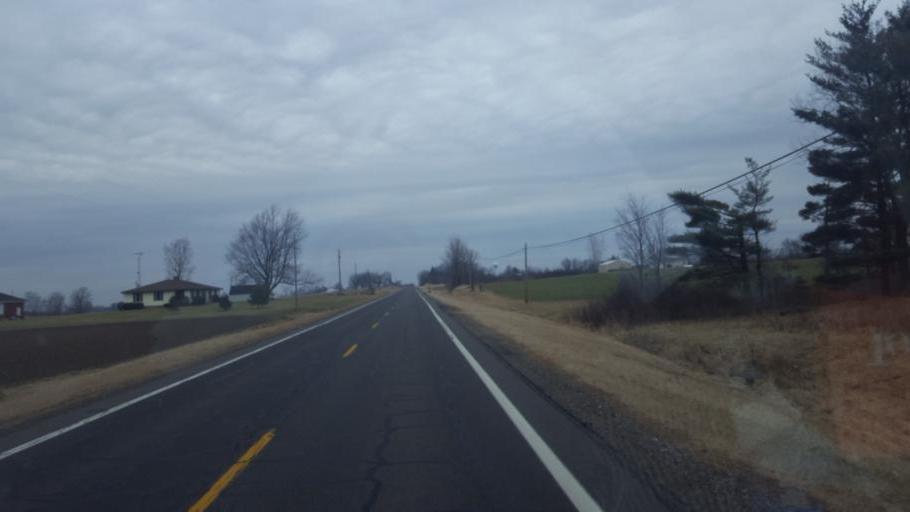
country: US
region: Ohio
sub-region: Crawford County
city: Galion
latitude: 40.6518
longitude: -82.8218
